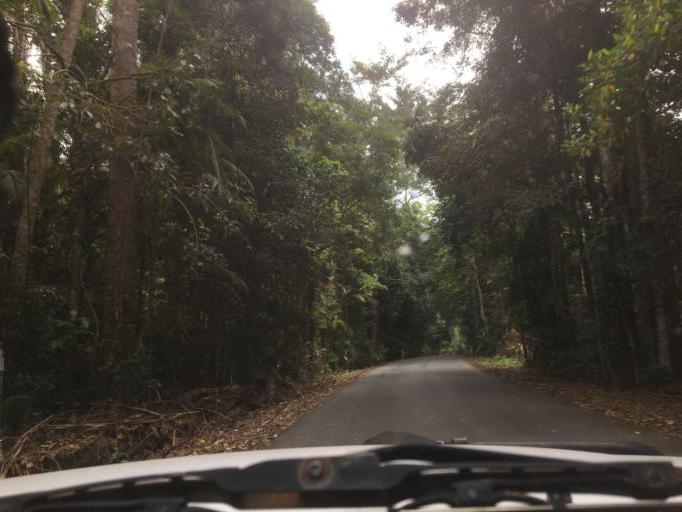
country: AU
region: Queensland
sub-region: Tablelands
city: Atherton
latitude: -17.2833
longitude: 145.6180
